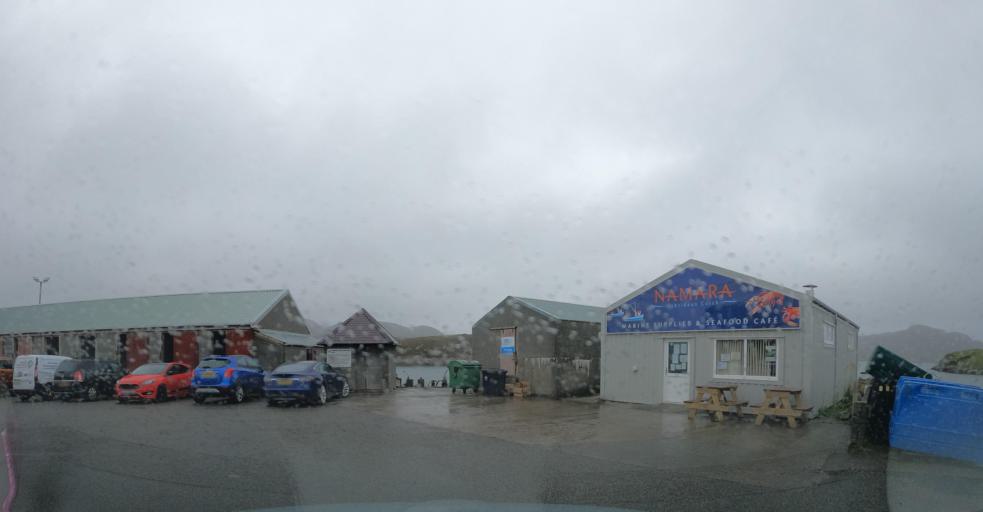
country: GB
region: Scotland
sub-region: Eilean Siar
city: Benbecula
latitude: 57.4809
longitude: -7.2047
